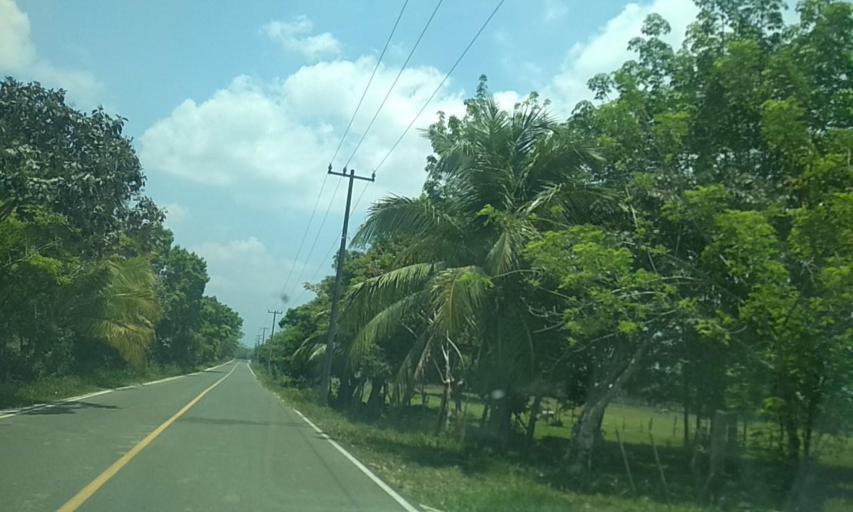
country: MX
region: Tabasco
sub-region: Huimanguillo
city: Francisco Rueda
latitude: 17.7489
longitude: -94.0392
